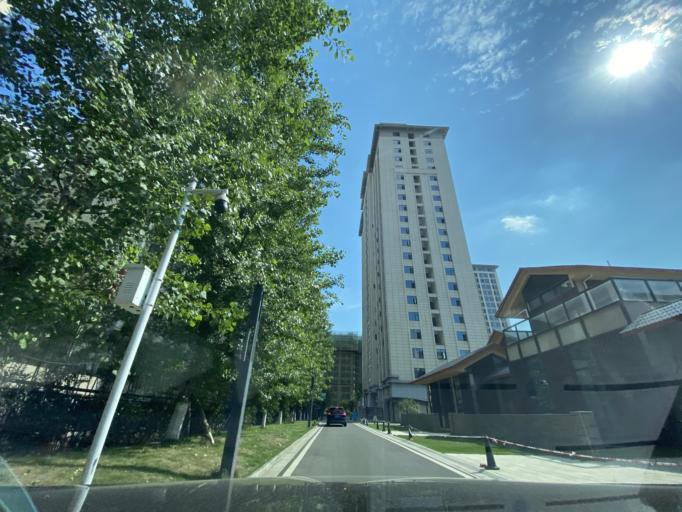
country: CN
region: Sichuan
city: Yanjiang
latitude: 30.1030
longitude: 104.6698
